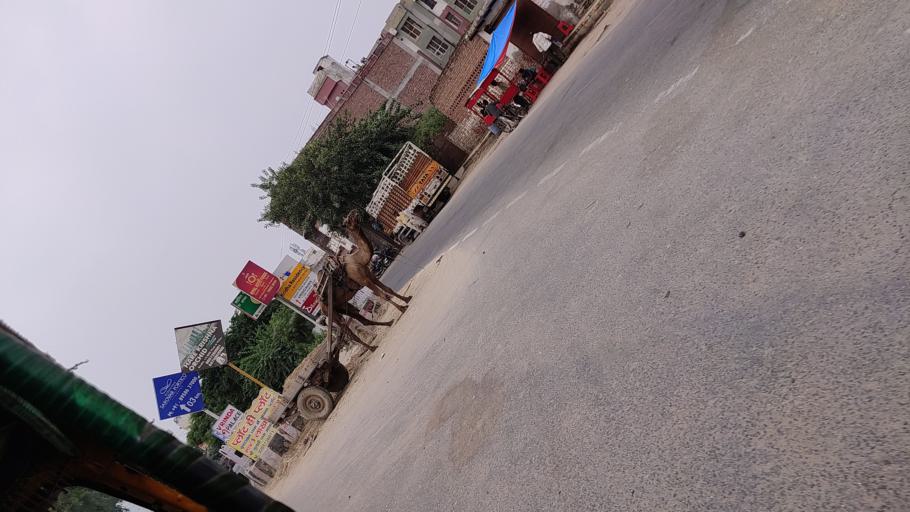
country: IN
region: Uttar Pradesh
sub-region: Mathura
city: Vrindavan
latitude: 27.5657
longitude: 77.6766
